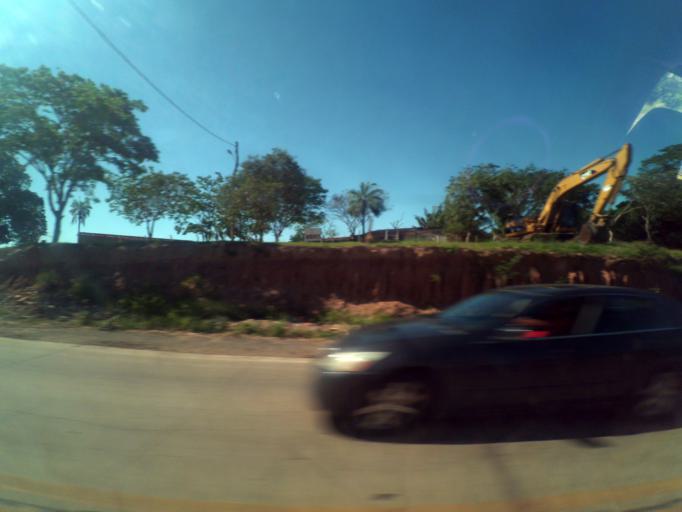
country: BO
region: Santa Cruz
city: Santa Cruz de la Sierra
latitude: -17.7616
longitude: -63.2289
